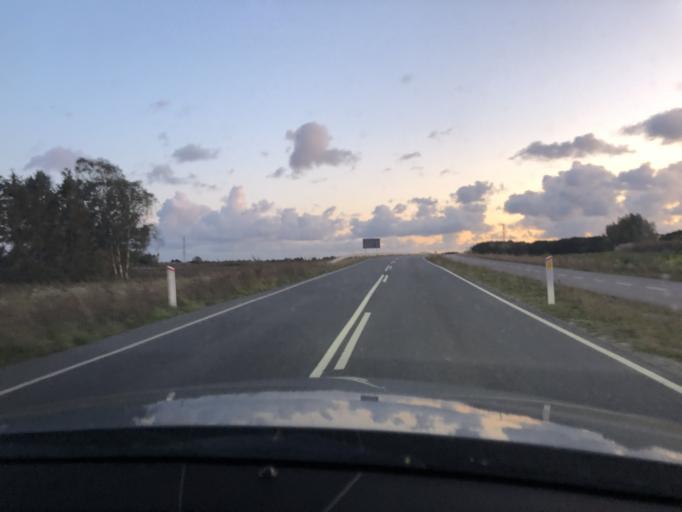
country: DK
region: Zealand
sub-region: Holbaek Kommune
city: Holbaek
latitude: 55.6613
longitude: 11.6195
